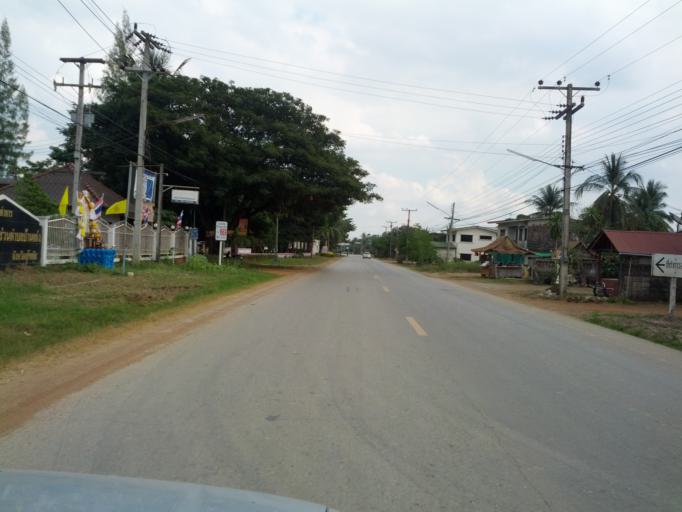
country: TH
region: Sukhothai
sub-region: Amphoe Si Satchanalai
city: Si Satchanalai
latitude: 17.4306
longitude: 99.6908
